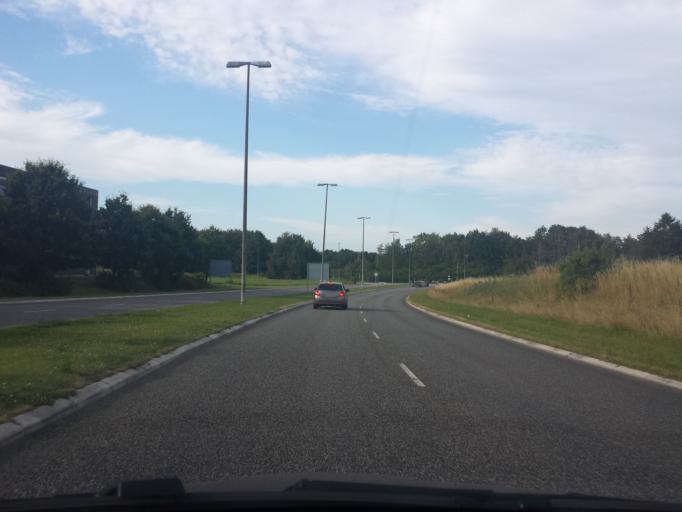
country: DK
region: Capital Region
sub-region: Ballerup Kommune
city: Ballerup
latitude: 55.7401
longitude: 12.3918
